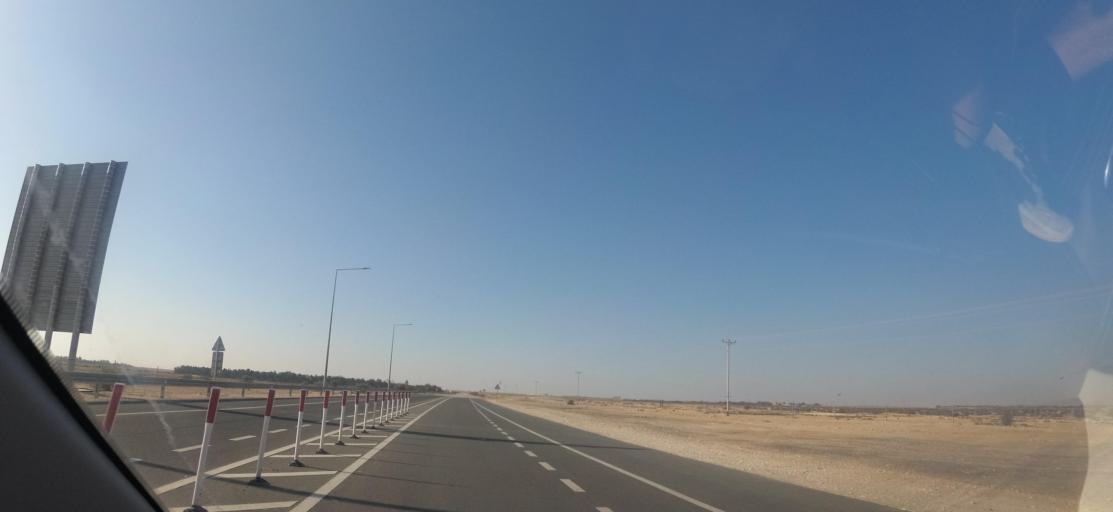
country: QA
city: Al Ghuwayriyah
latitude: 25.8488
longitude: 51.2650
